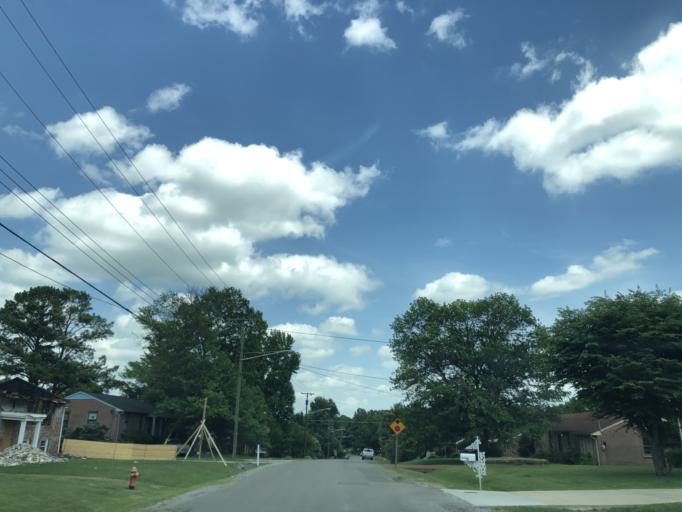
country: US
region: Tennessee
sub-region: Davidson County
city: Oak Hill
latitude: 36.0824
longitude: -86.7525
